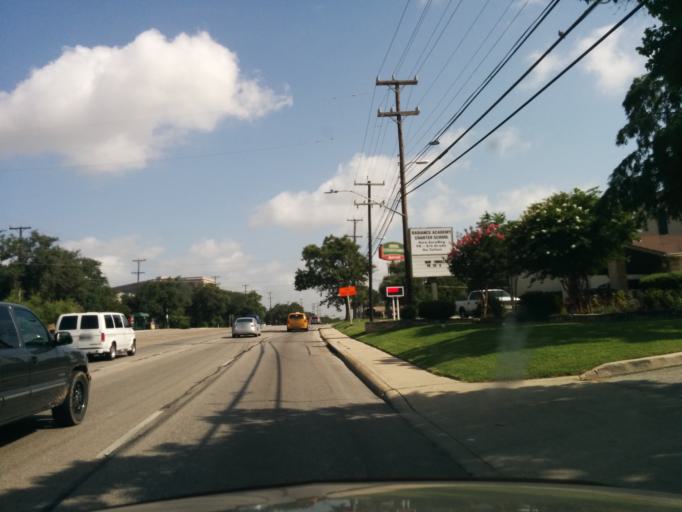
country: US
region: Texas
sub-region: Bexar County
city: Balcones Heights
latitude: 29.5165
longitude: -98.5720
